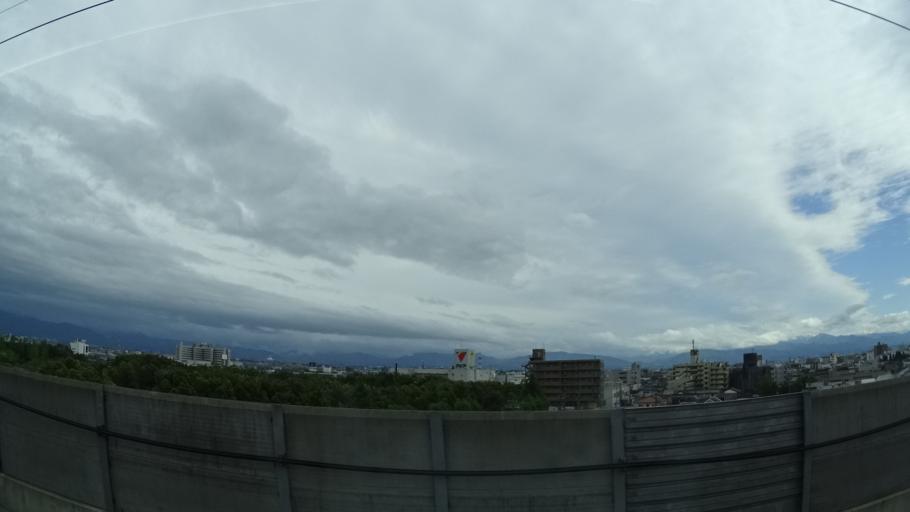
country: JP
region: Toyama
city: Toyama-shi
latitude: 36.6990
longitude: 137.2286
